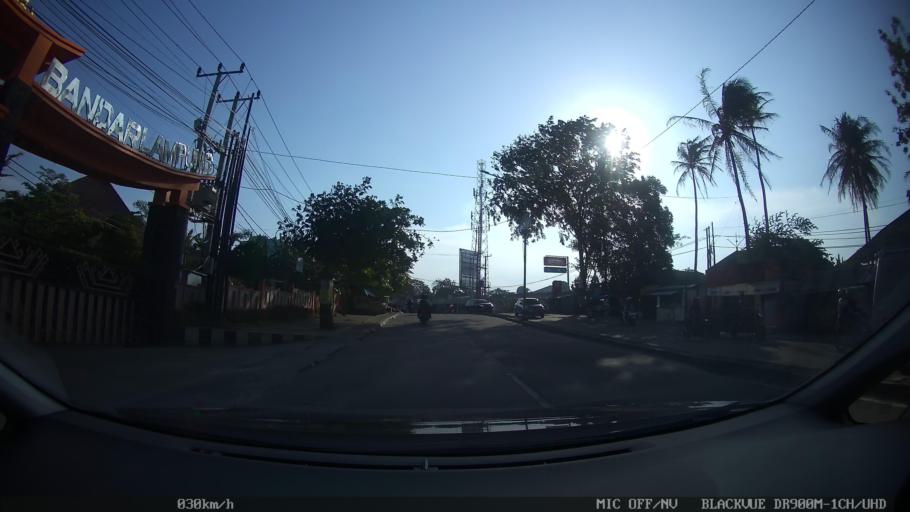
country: ID
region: Lampung
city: Kedaton
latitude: -5.3766
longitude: 105.2219
